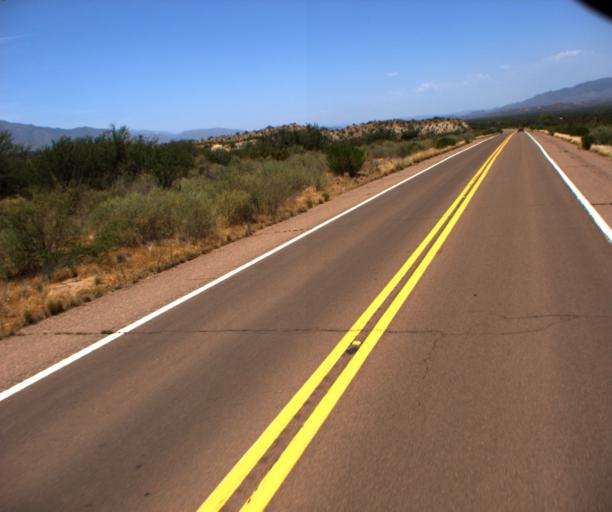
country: US
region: Arizona
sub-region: Gila County
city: Tonto Basin
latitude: 33.8136
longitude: -111.2889
